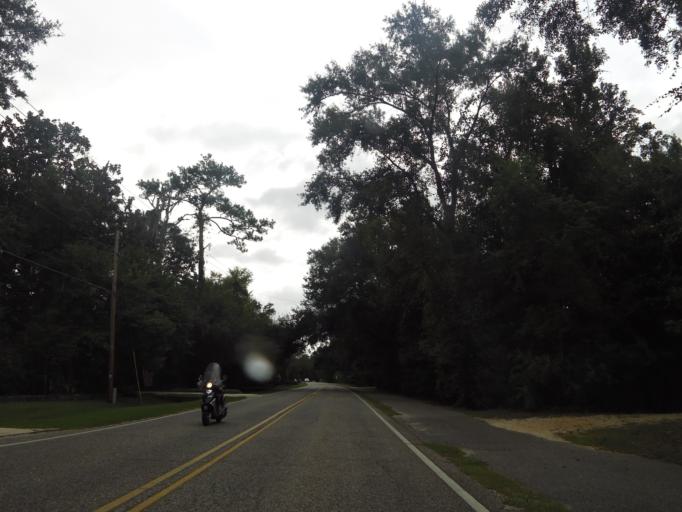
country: US
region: Alabama
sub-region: Baldwin County
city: Point Clear
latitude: 30.4795
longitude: -87.9244
